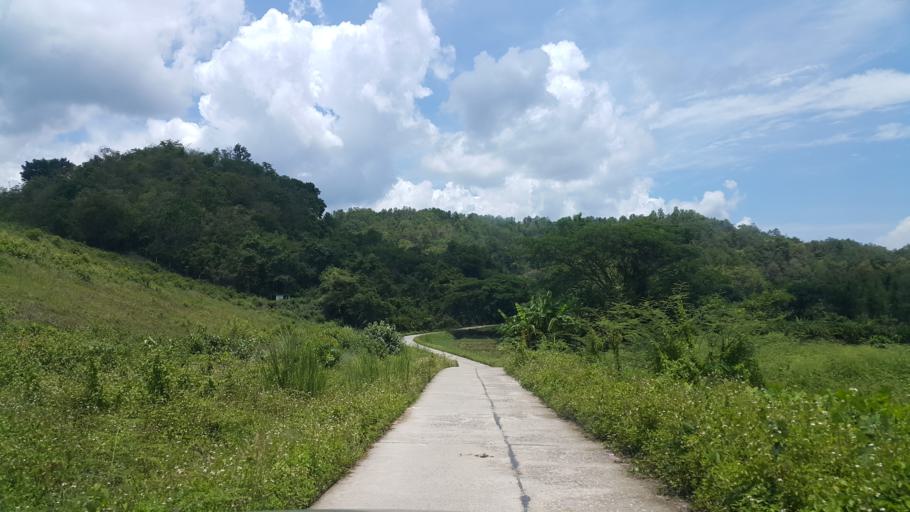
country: TH
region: Phayao
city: Phayao
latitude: 19.1855
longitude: 99.8017
